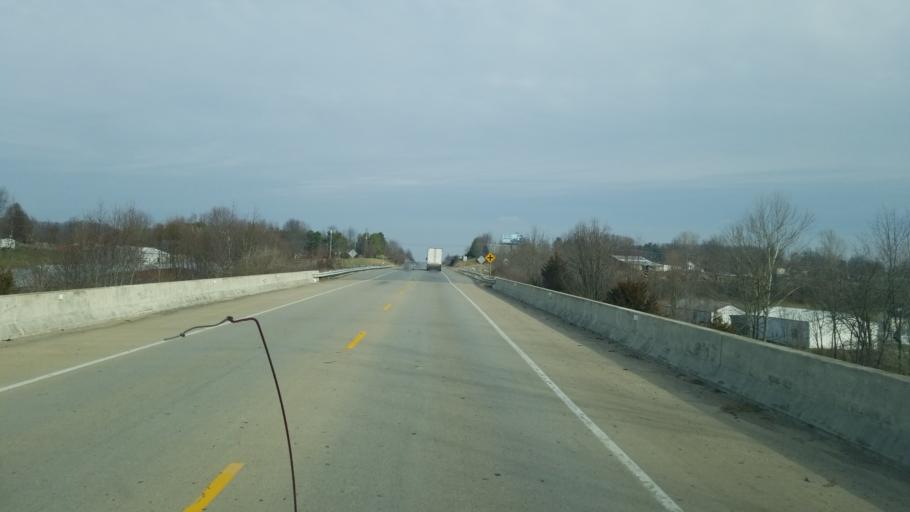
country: US
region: Kentucky
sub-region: Boyle County
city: Junction City
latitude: 37.5403
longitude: -84.8032
